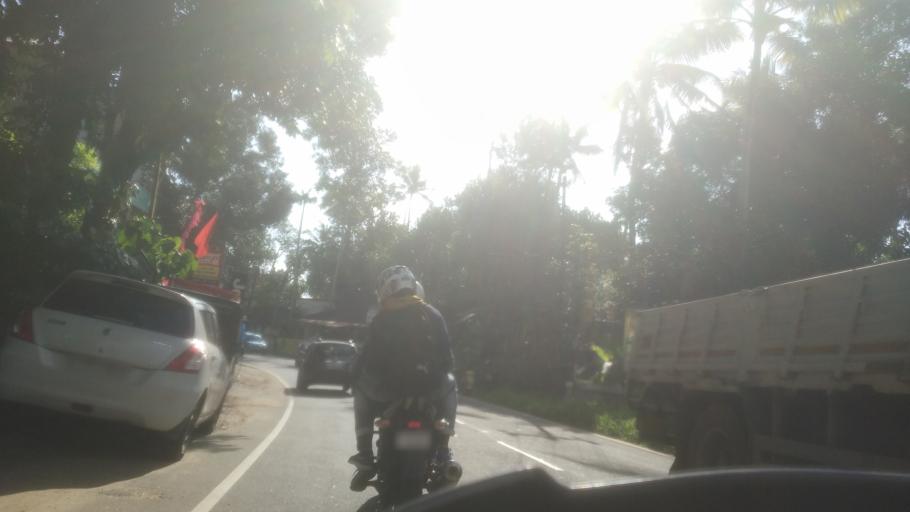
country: IN
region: Kerala
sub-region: Ernakulam
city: Muvattupula
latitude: 9.9894
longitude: 76.5708
